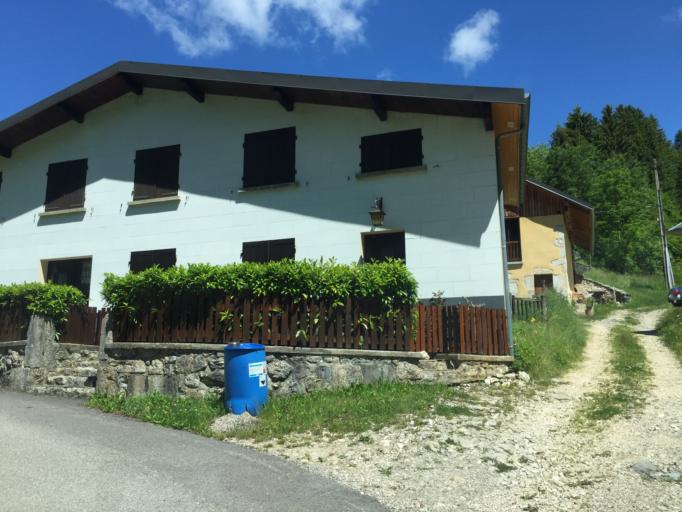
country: FR
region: Rhone-Alpes
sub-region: Departement de la Savoie
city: Saint-Baldoph
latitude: 45.4686
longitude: 5.8972
